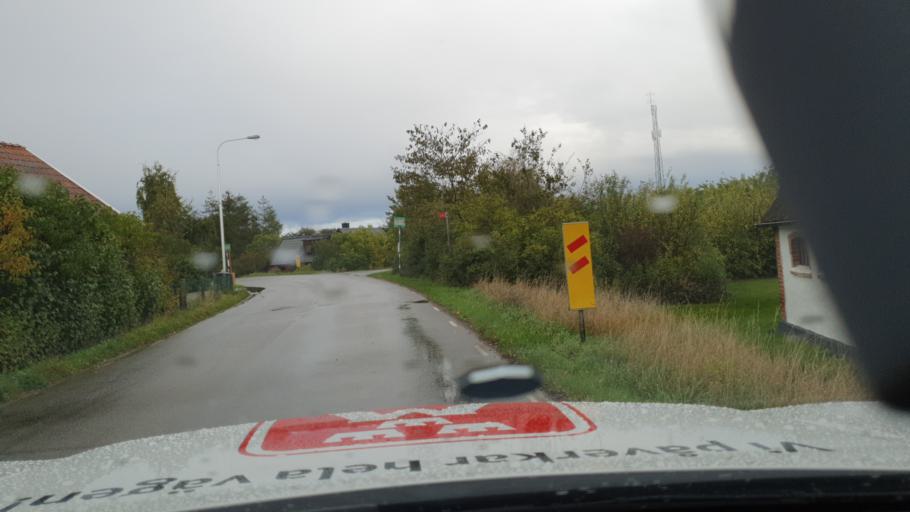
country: SE
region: Skane
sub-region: Malmo
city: Oxie
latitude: 55.5240
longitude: 13.0646
